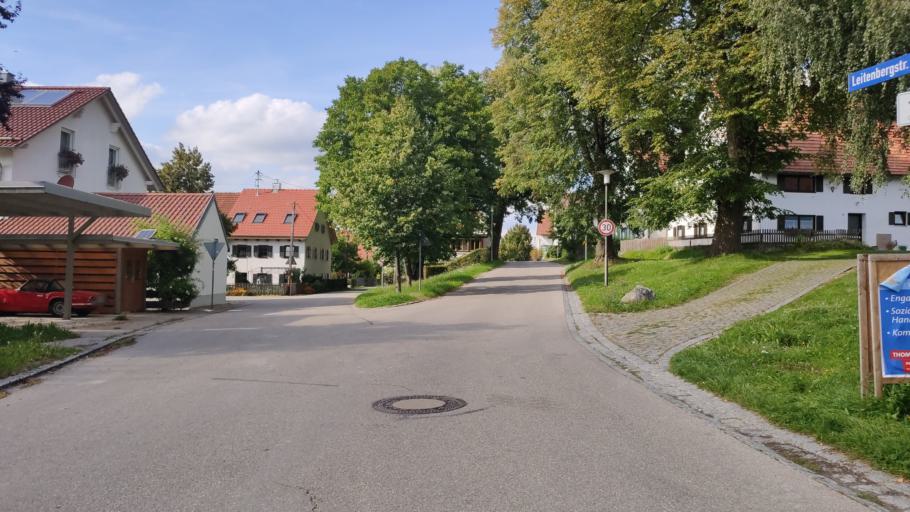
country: DE
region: Bavaria
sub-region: Upper Bavaria
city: Kaufering
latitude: 48.0931
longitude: 10.8748
